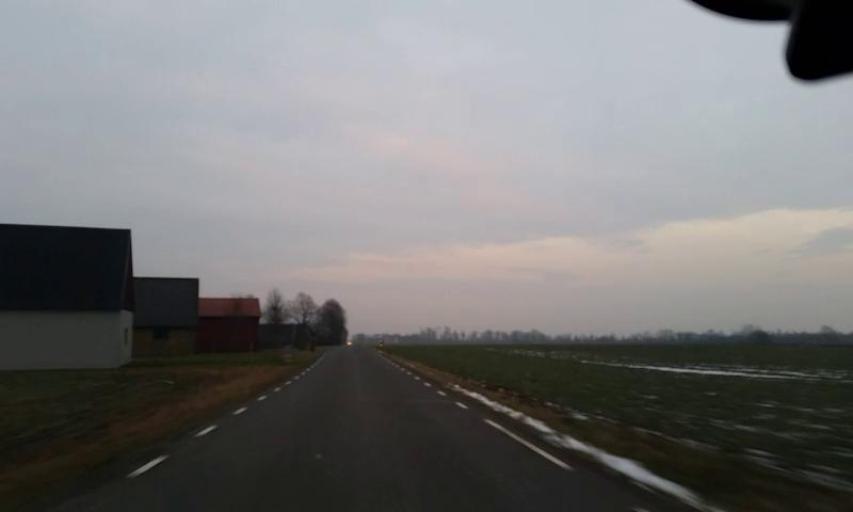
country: SE
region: Skane
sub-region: Angelholms Kommun
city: AEngelholm
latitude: 56.2793
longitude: 12.8642
